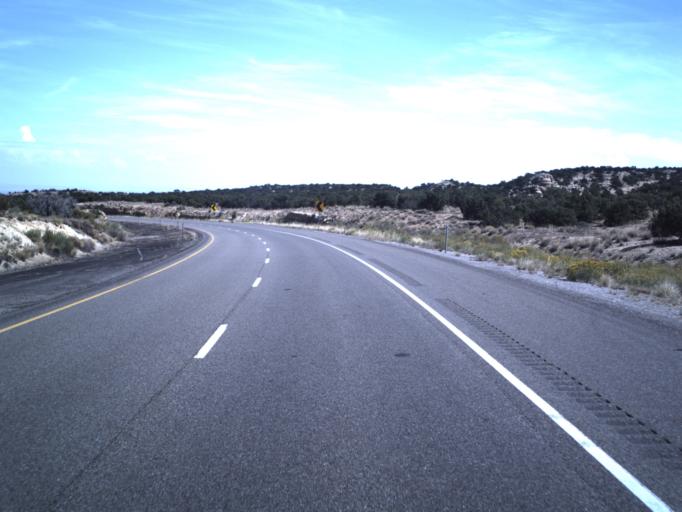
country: US
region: Utah
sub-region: Emery County
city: Castle Dale
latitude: 38.9133
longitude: -110.5098
